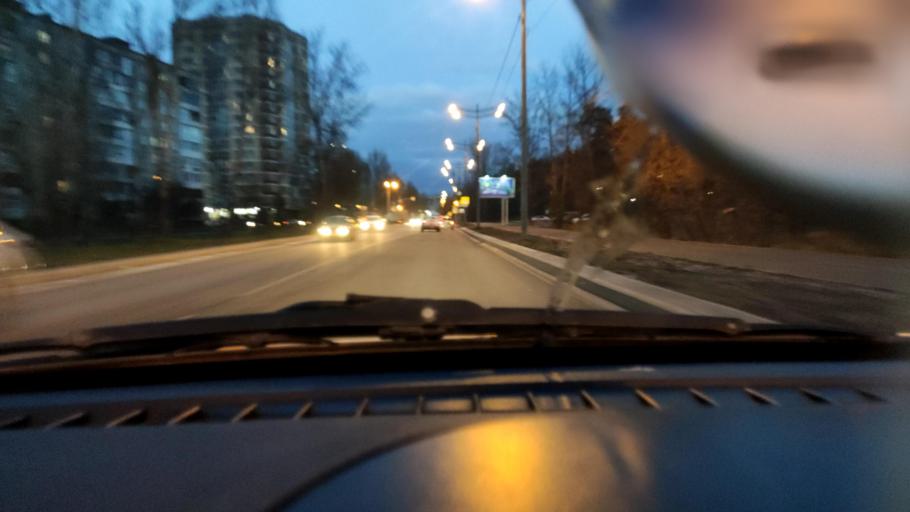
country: RU
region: Perm
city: Kondratovo
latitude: 57.9932
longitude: 56.1551
